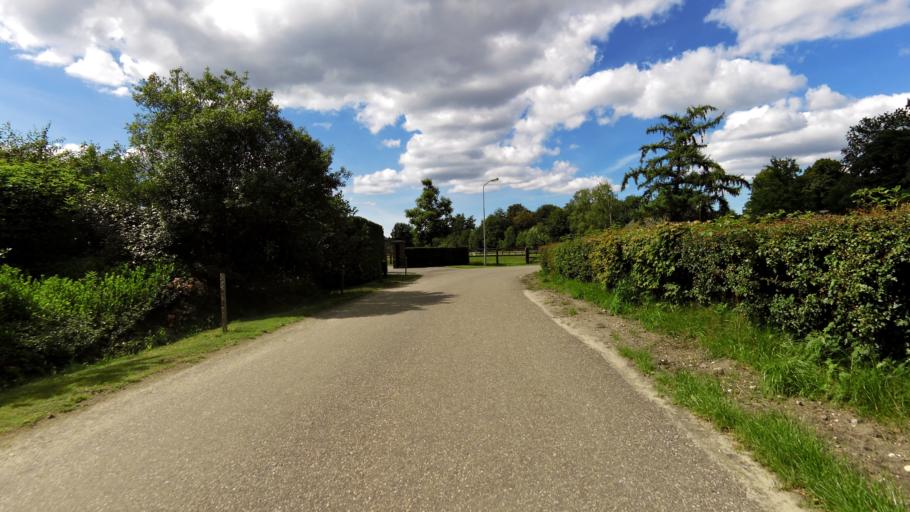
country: NL
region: Gelderland
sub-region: Gemeente Epe
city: Vaassen
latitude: 52.2559
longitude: 5.9381
